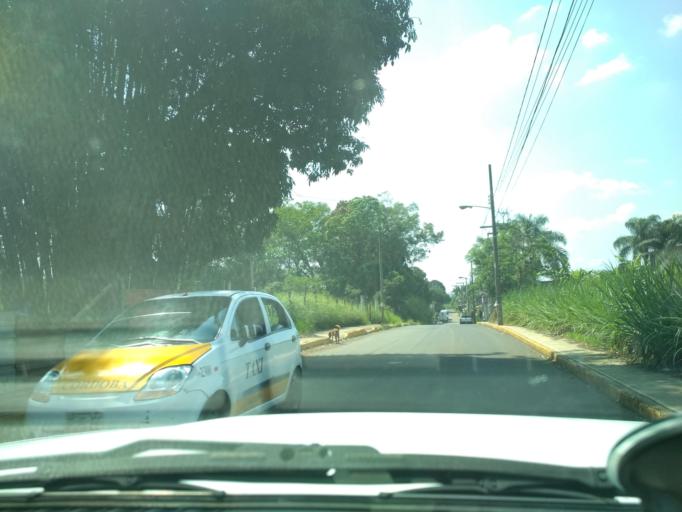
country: MX
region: Veracruz
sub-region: Fortin
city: Cordoba (Santa Leticia)
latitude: 18.9155
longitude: -96.9742
